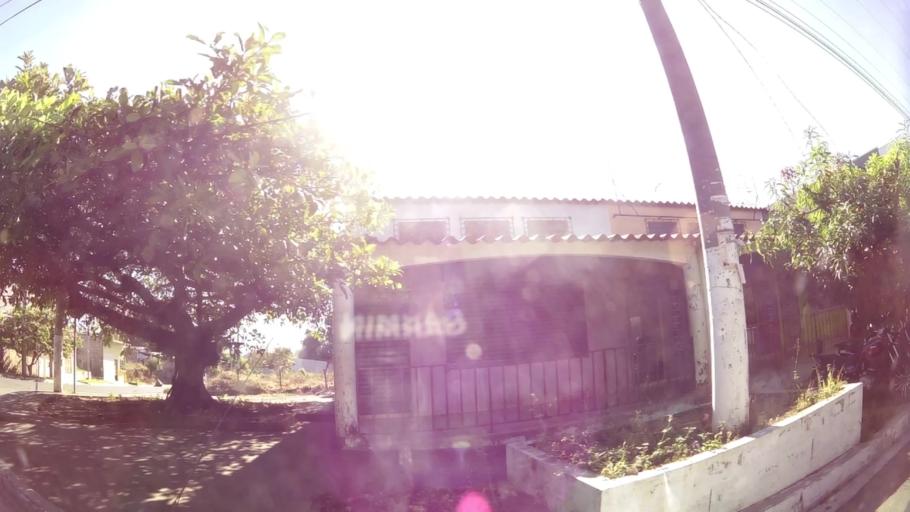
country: SV
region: Sonsonate
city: Sonzacate
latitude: 13.7391
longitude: -89.7156
